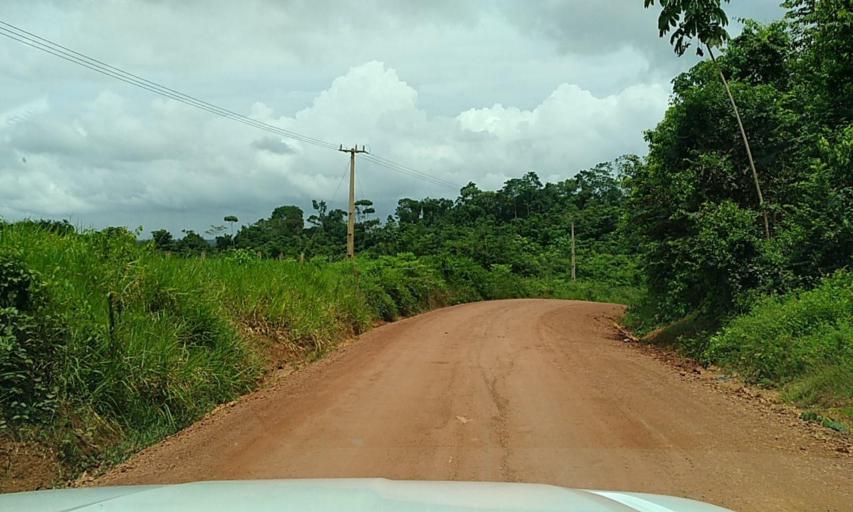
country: BR
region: Para
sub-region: Senador Jose Porfirio
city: Senador Jose Porfirio
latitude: -2.6604
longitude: -51.8431
